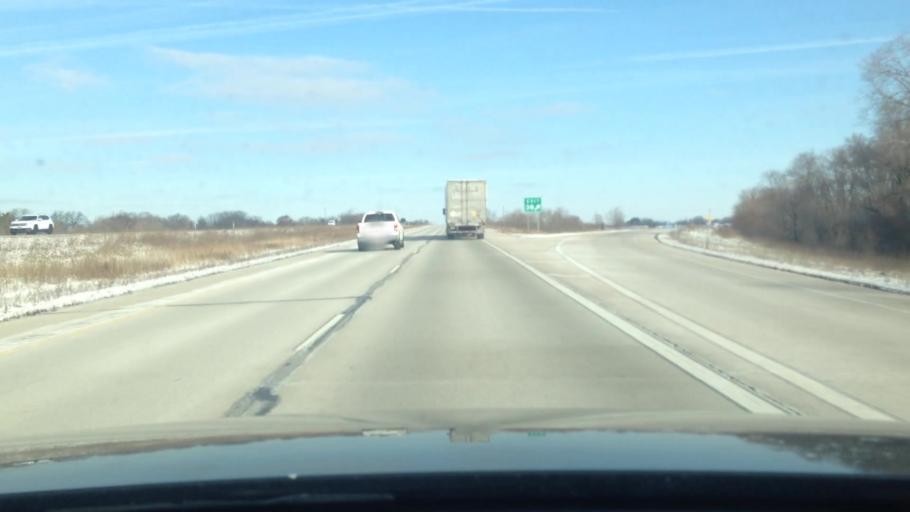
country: US
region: Wisconsin
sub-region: Walworth County
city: East Troy
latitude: 42.7872
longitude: -88.3871
